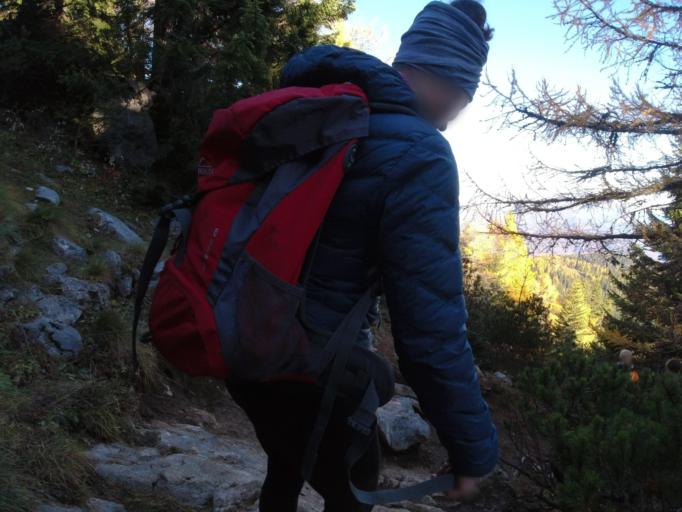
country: AT
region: Carinthia
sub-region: Politischer Bezirk Volkermarkt
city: Gallizien
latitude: 46.5028
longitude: 14.5039
